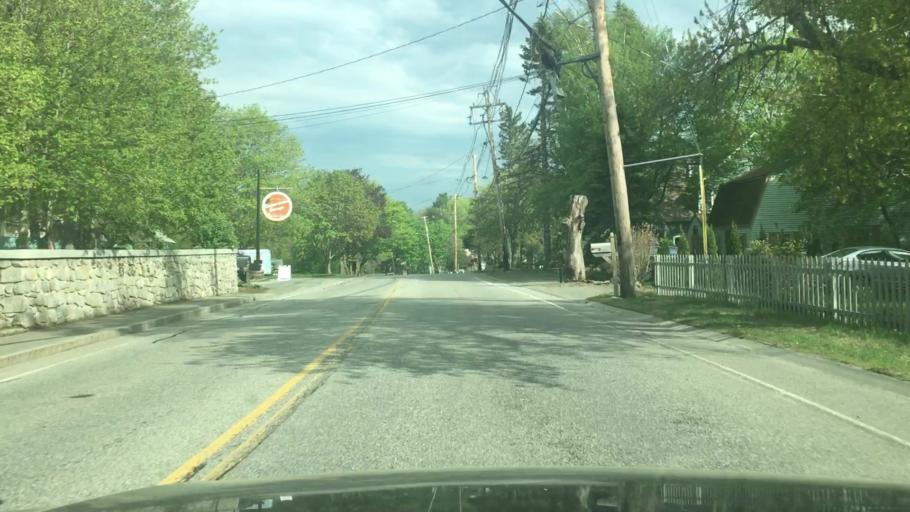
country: US
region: Massachusetts
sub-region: Middlesex County
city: North Reading
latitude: 42.5742
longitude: -71.1043
